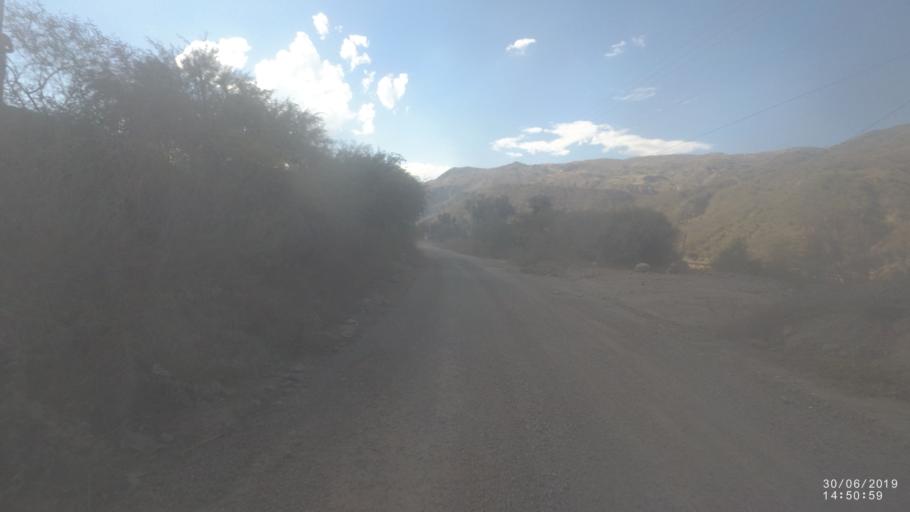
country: BO
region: Cochabamba
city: Irpa Irpa
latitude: -17.7744
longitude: -66.3439
